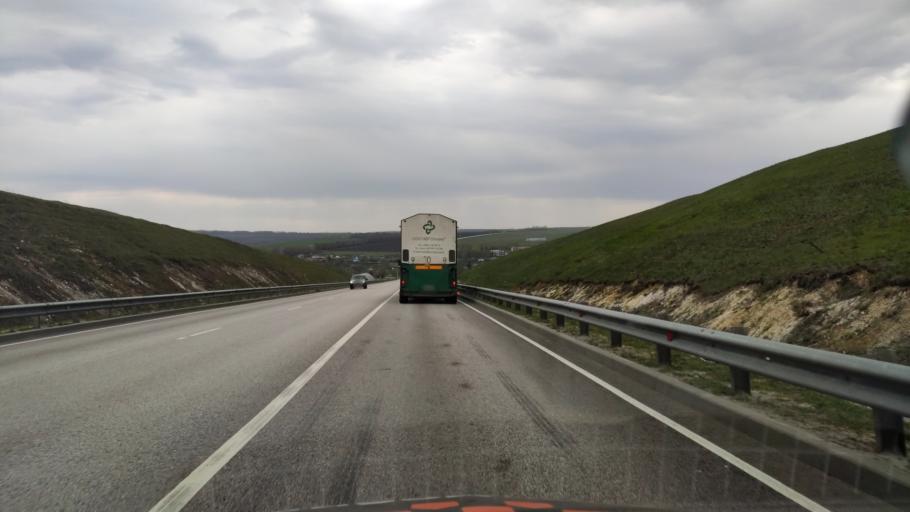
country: RU
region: Voronezj
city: Nizhnedevitsk
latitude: 51.5961
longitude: 38.5955
